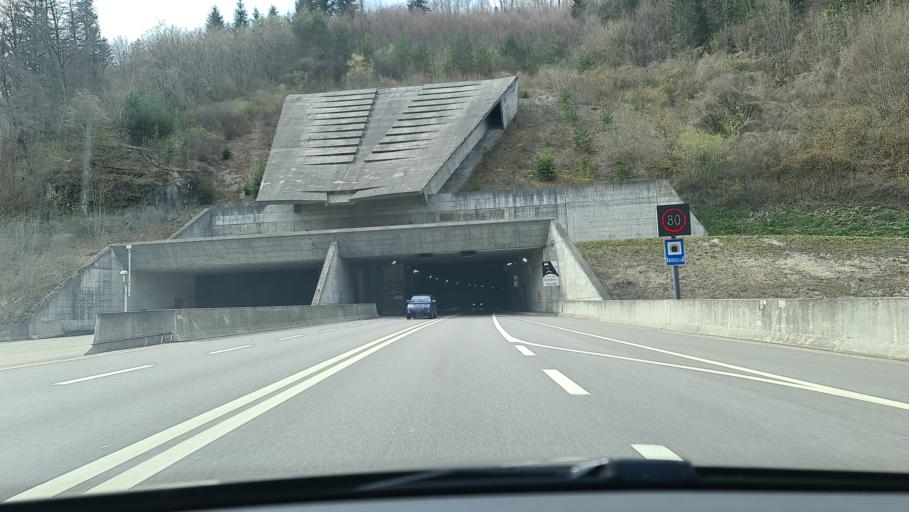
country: CH
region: Jura
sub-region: Delemont District
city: Glovelier
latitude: 47.3701
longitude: 7.1762
